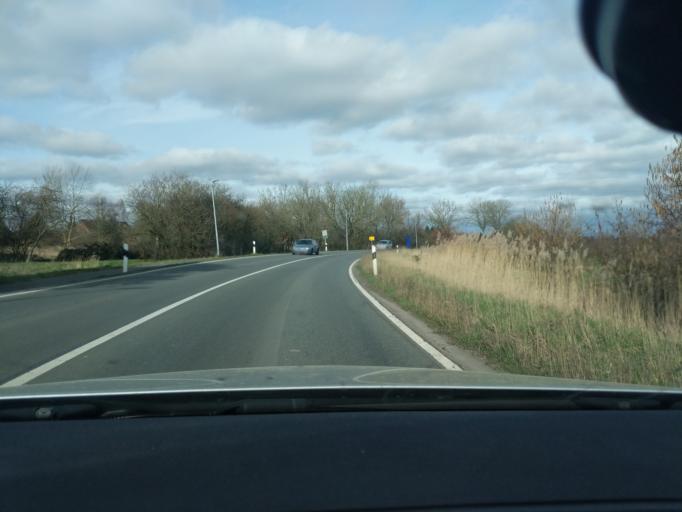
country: DE
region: Lower Saxony
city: Stade
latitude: 53.6570
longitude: 9.4760
